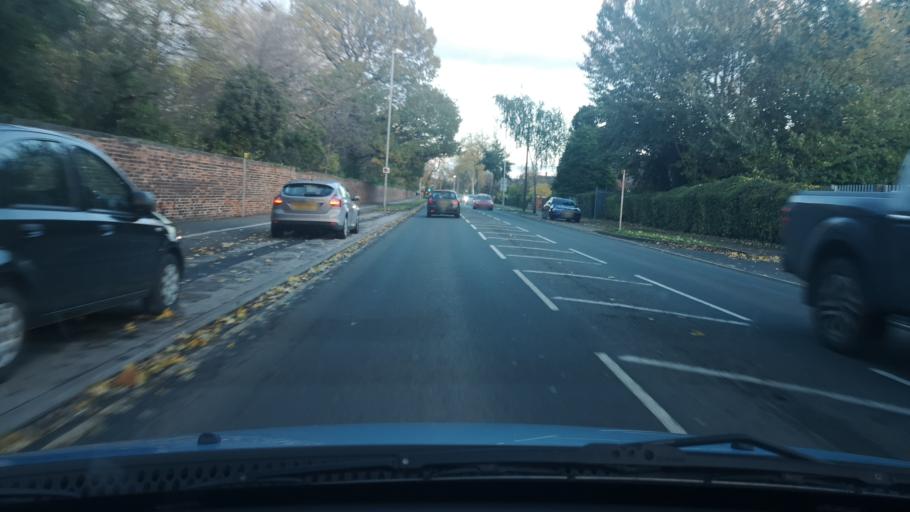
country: GB
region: England
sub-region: City and Borough of Wakefield
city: Wakefield
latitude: 53.6708
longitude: -1.5152
